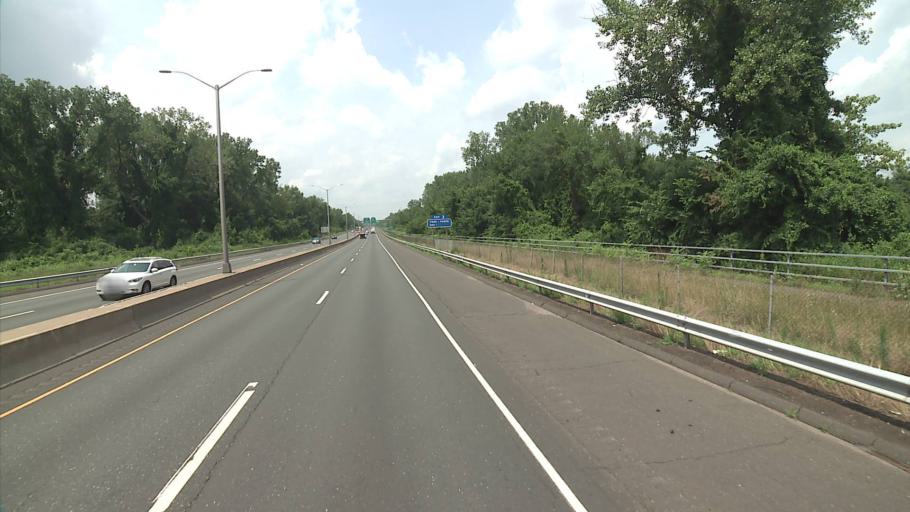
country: US
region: Connecticut
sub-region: Hartford County
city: South Windsor
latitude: 41.8090
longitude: -72.6283
